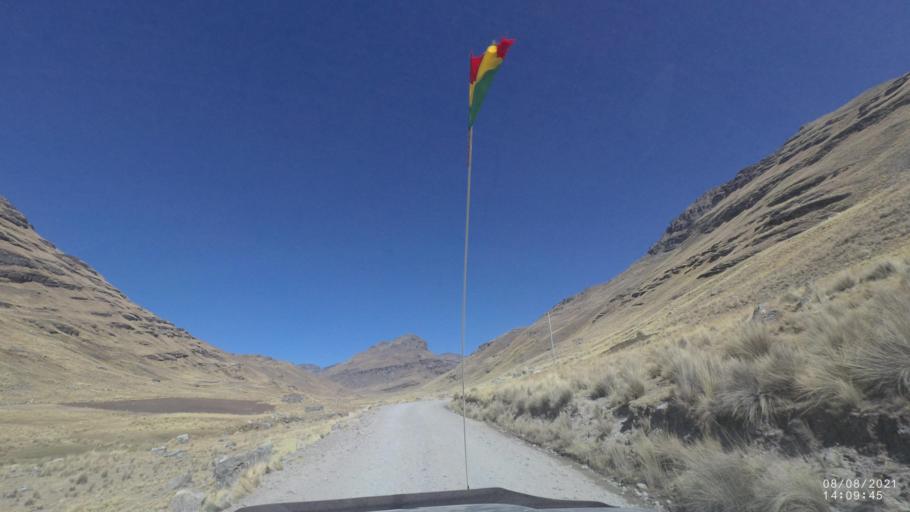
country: BO
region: Cochabamba
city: Sipe Sipe
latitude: -17.1475
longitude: -66.4367
